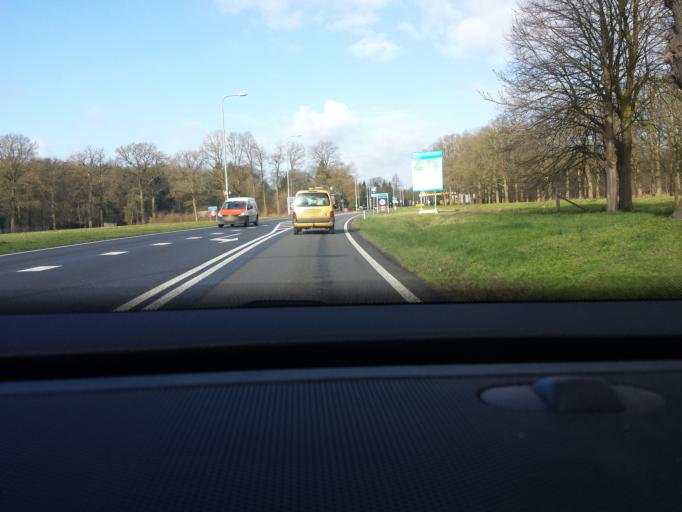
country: NL
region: Gelderland
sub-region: Gemeente Zutphen
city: Warnsveld
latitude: 52.1433
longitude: 6.2428
